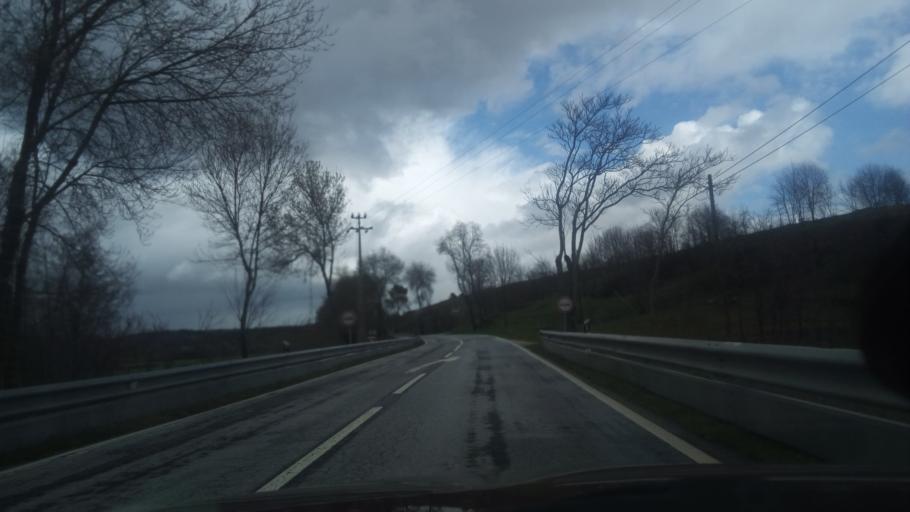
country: PT
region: Guarda
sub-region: Fornos de Algodres
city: Fornos de Algodres
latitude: 40.5686
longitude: -7.4692
